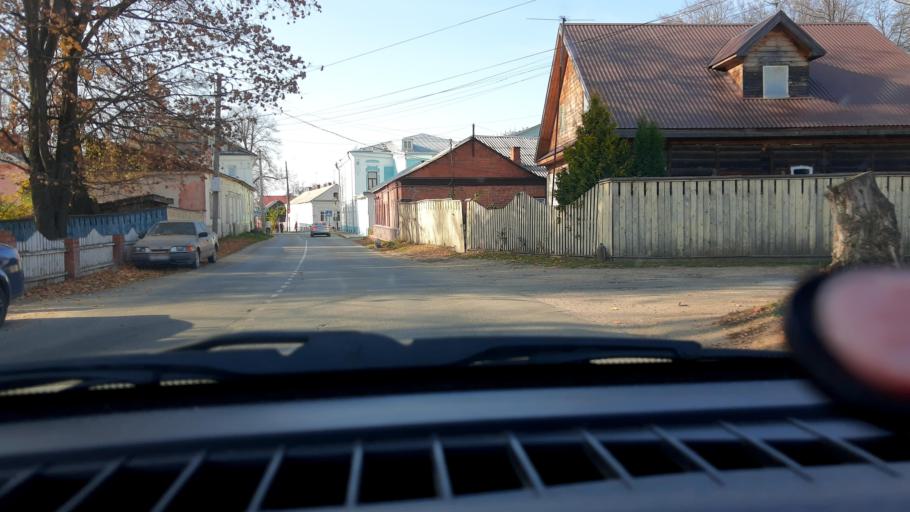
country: RU
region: Nizjnij Novgorod
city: Gorodets
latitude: 56.6430
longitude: 43.4700
